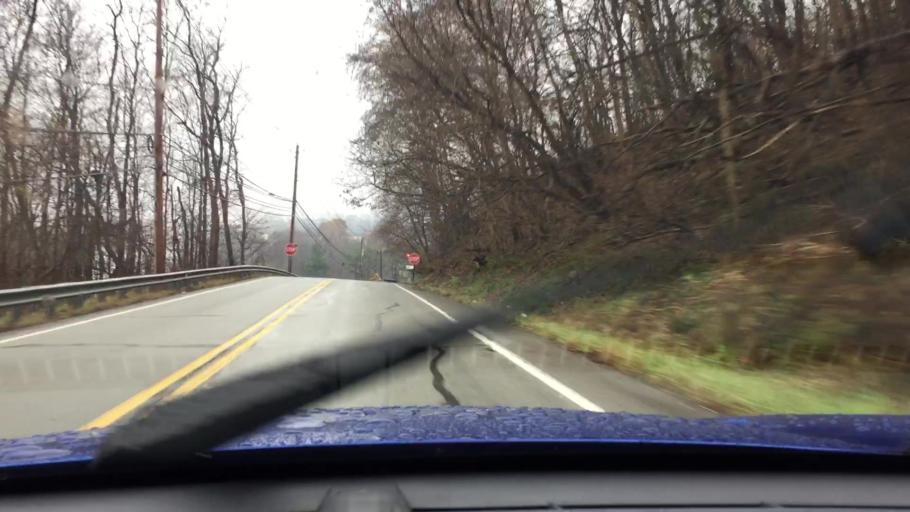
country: US
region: Pennsylvania
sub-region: Washington County
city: Canonsburg
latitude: 40.2834
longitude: -80.1552
